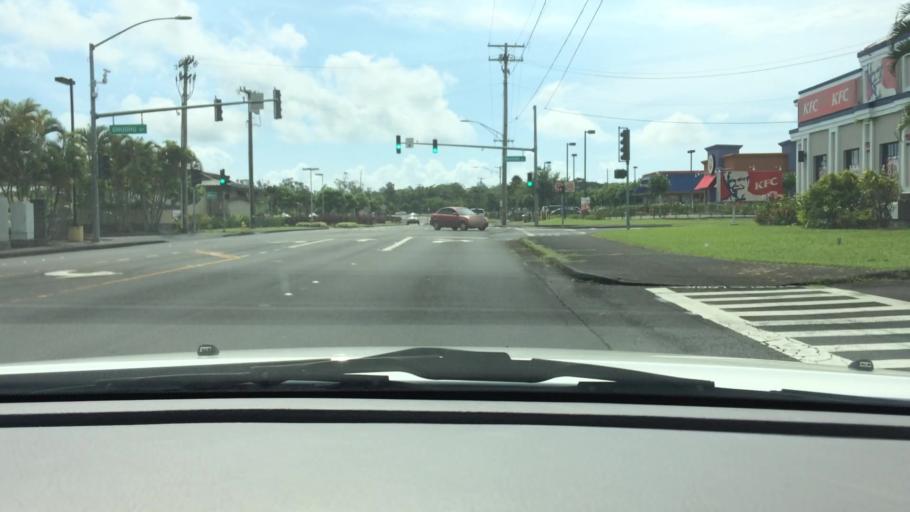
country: US
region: Hawaii
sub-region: Hawaii County
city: Hilo
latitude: 19.6992
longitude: -155.0619
